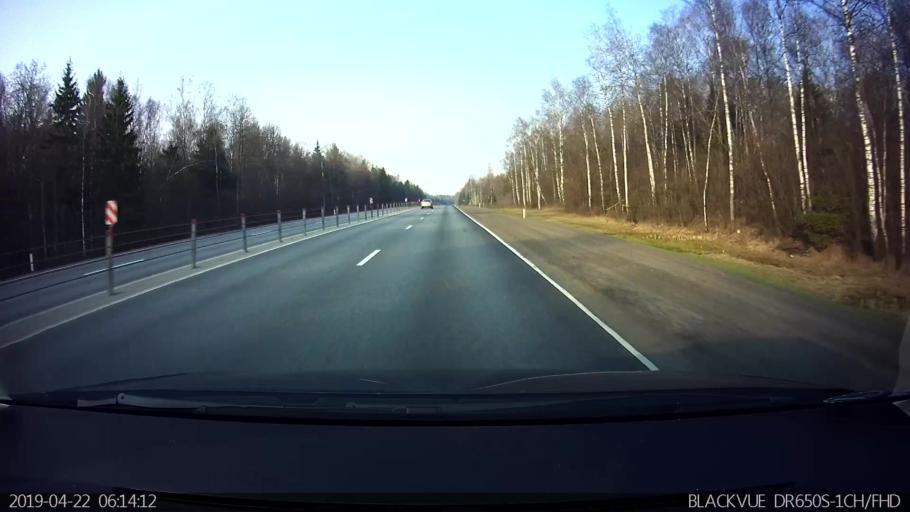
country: RU
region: Moskovskaya
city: Mozhaysk
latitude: 55.4638
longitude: 36.0840
